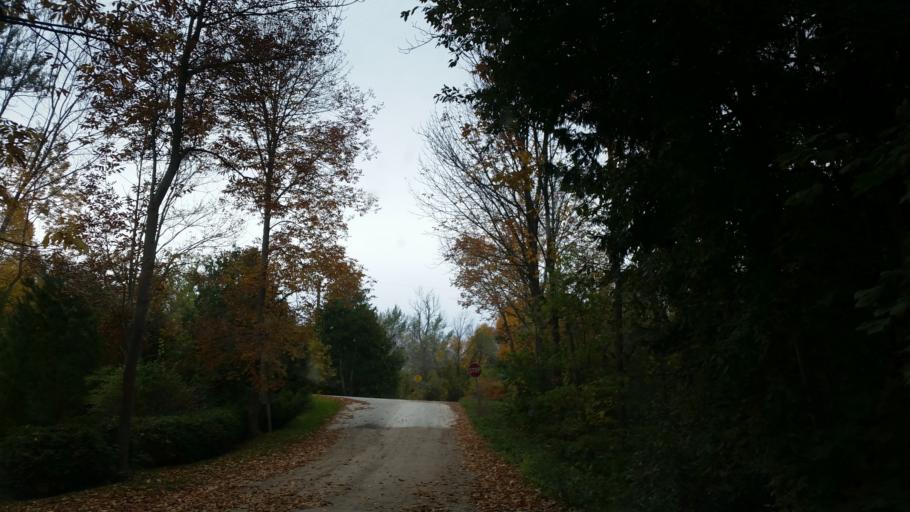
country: CA
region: Ontario
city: Goderich
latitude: 44.1207
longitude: -81.7002
